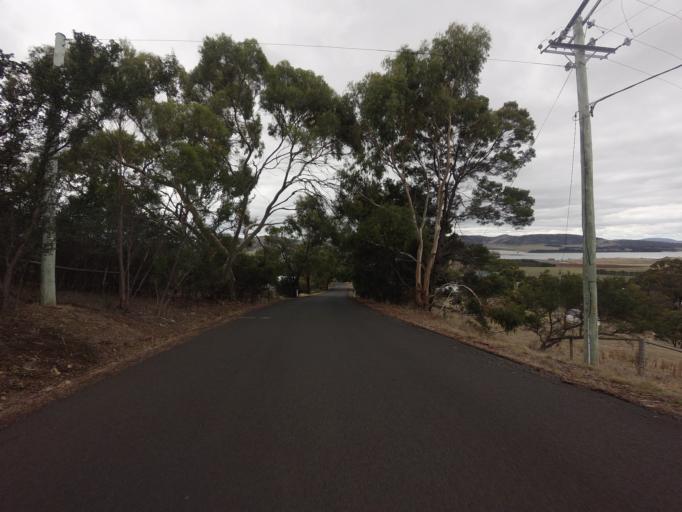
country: AU
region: Tasmania
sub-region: Clarence
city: Cambridge
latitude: -42.7880
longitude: 147.4102
